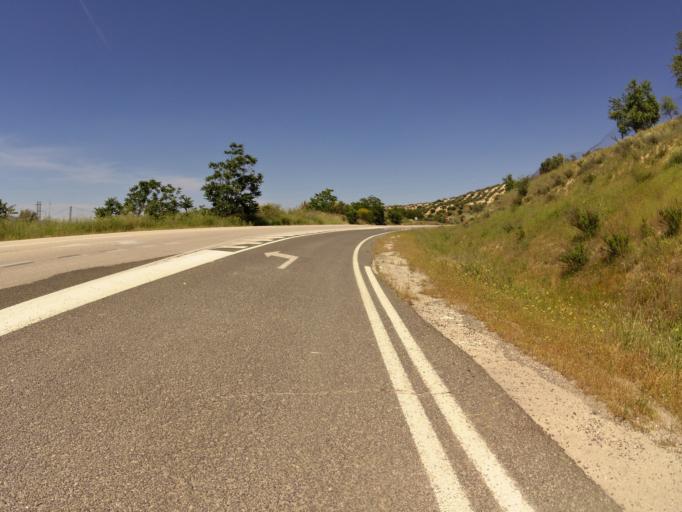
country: ES
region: Andalusia
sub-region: Provincia de Granada
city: Salar
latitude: 37.1698
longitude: -4.0867
